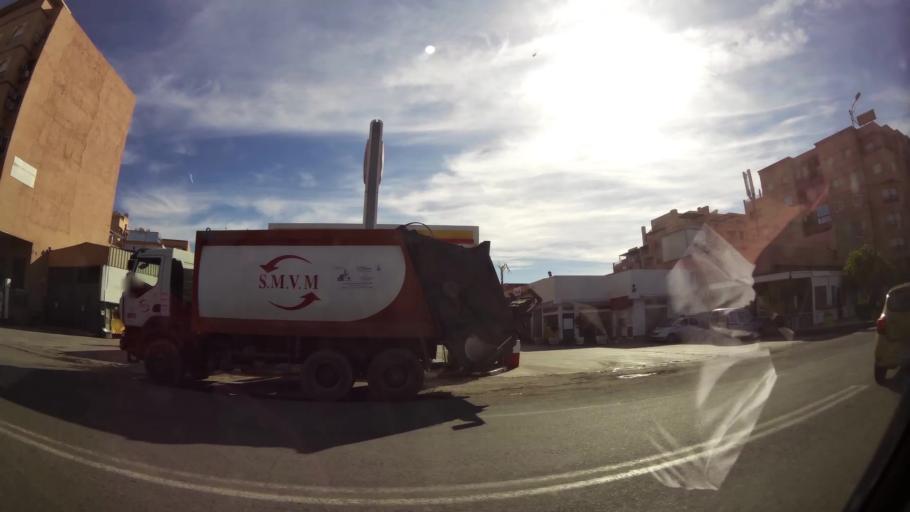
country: MA
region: Marrakech-Tensift-Al Haouz
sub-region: Marrakech
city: Marrakesh
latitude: 31.6565
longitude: -8.0215
